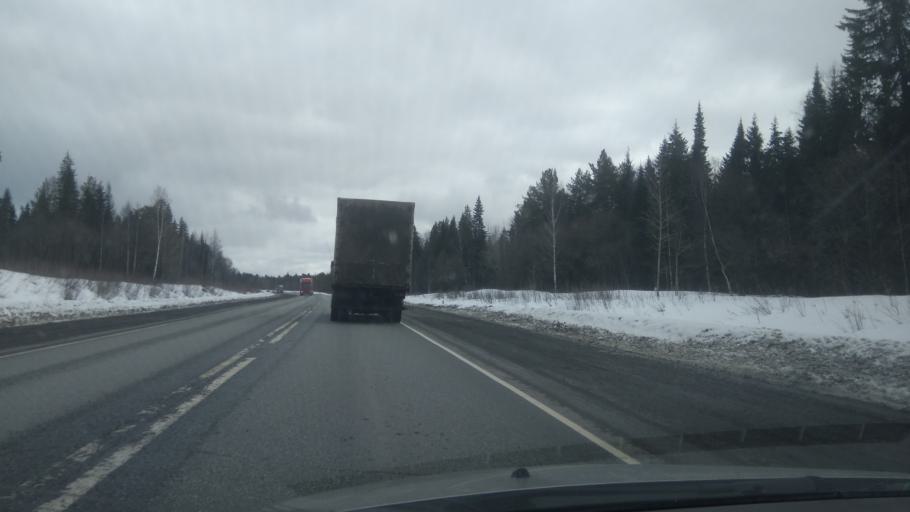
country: RU
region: Sverdlovsk
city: Atig
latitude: 56.7987
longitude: 59.3891
